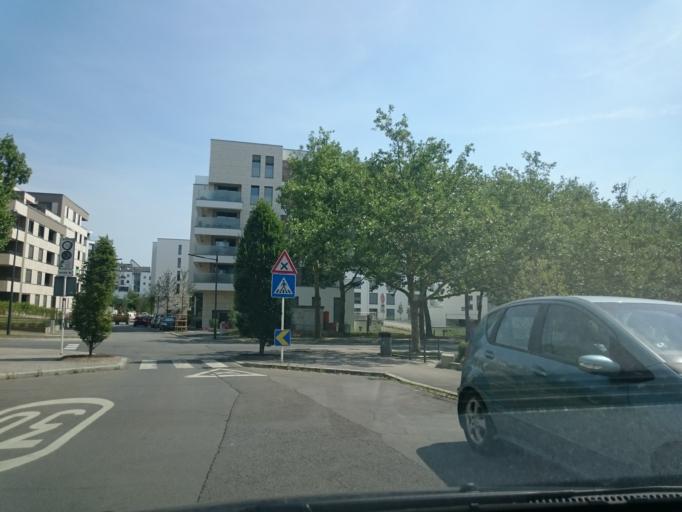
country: LU
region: Luxembourg
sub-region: Canton de Luxembourg
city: Luxembourg
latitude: 49.6044
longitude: 6.1037
